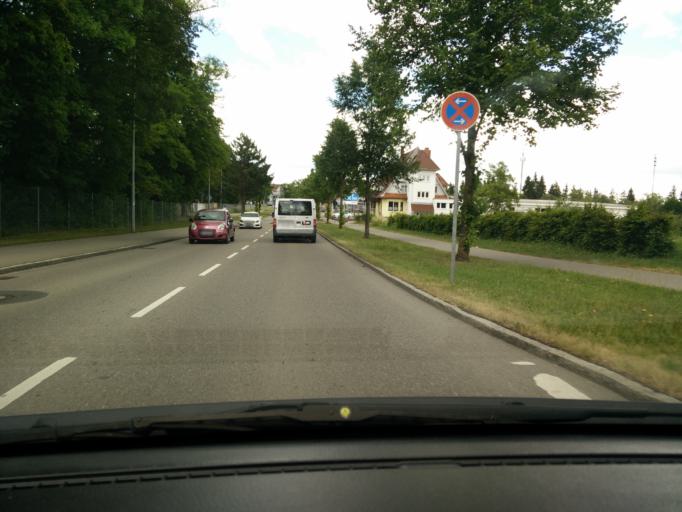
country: DE
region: Baden-Wuerttemberg
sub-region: Freiburg Region
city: Bad Durrheim
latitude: 48.0527
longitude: 8.5299
